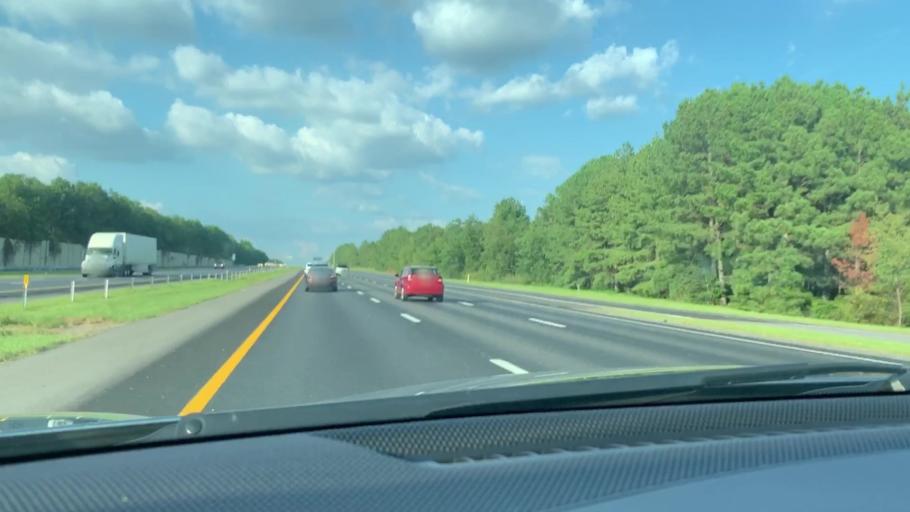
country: US
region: South Carolina
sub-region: Richland County
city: Woodfield
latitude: 34.0239
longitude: -80.9448
